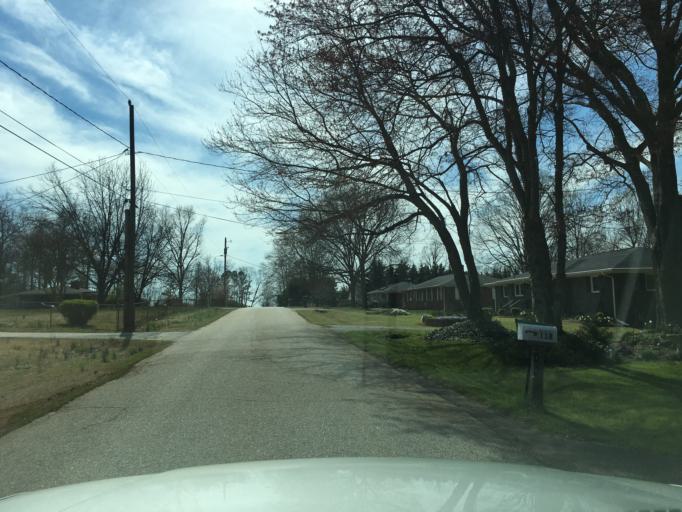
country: US
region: South Carolina
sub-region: Spartanburg County
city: Lyman
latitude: 34.9172
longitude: -82.1168
